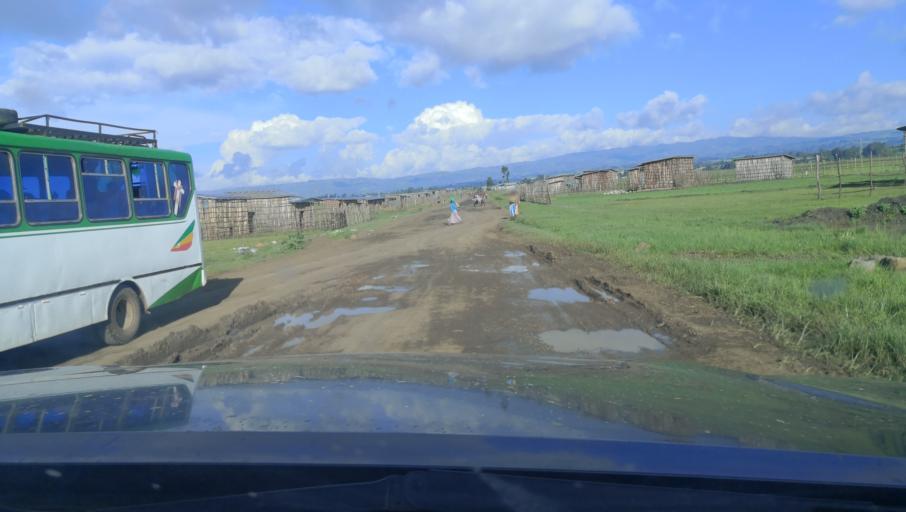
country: ET
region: Oromiya
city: Tulu Bolo
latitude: 8.4762
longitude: 38.2377
